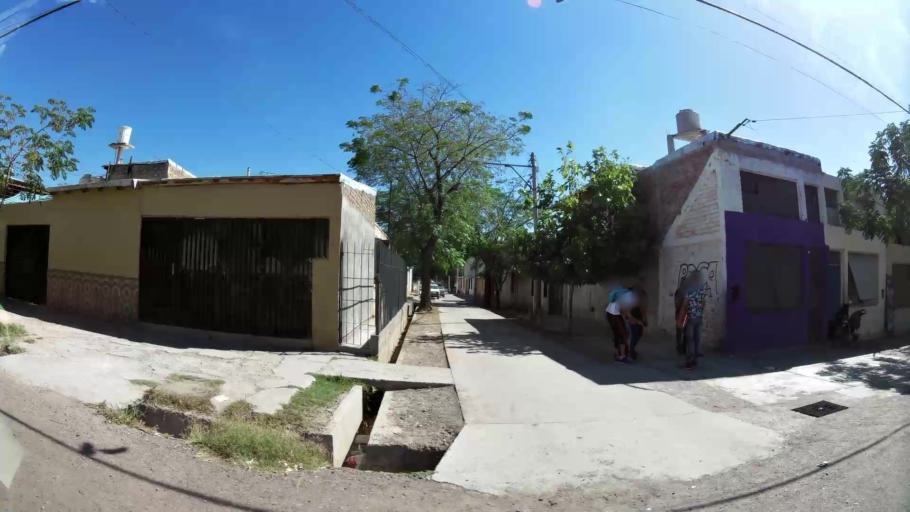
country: AR
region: Mendoza
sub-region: Departamento de Godoy Cruz
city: Godoy Cruz
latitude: -32.9059
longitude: -68.8683
